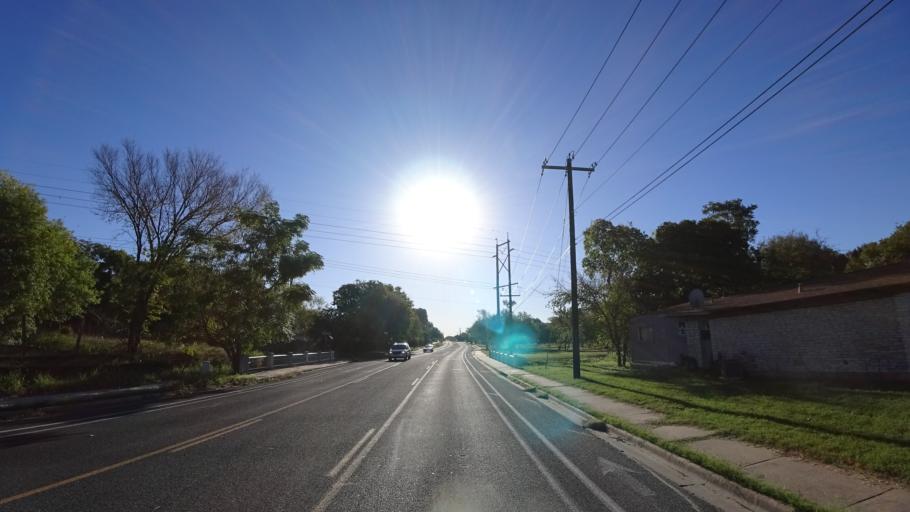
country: US
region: Texas
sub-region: Travis County
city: Austin
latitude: 30.2973
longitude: -97.6855
